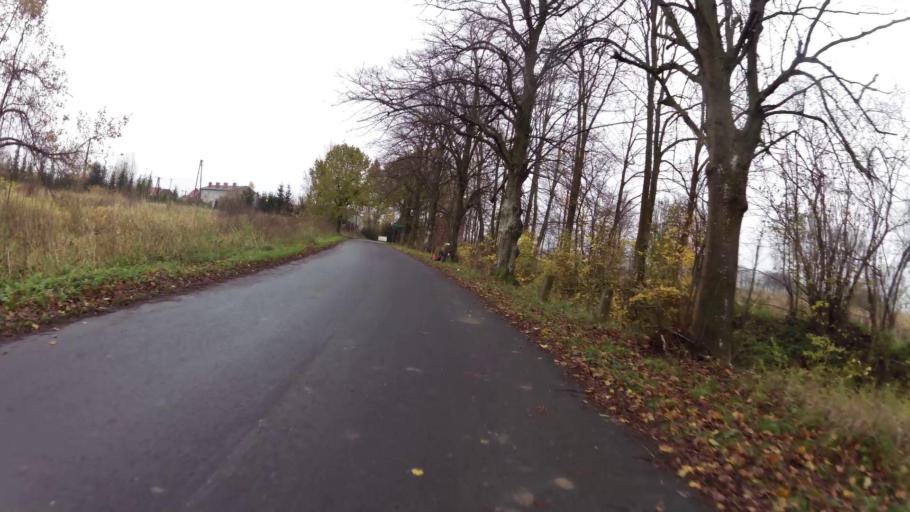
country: PL
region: West Pomeranian Voivodeship
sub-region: Powiat koszalinski
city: Mielno
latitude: 54.2387
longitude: 16.1062
